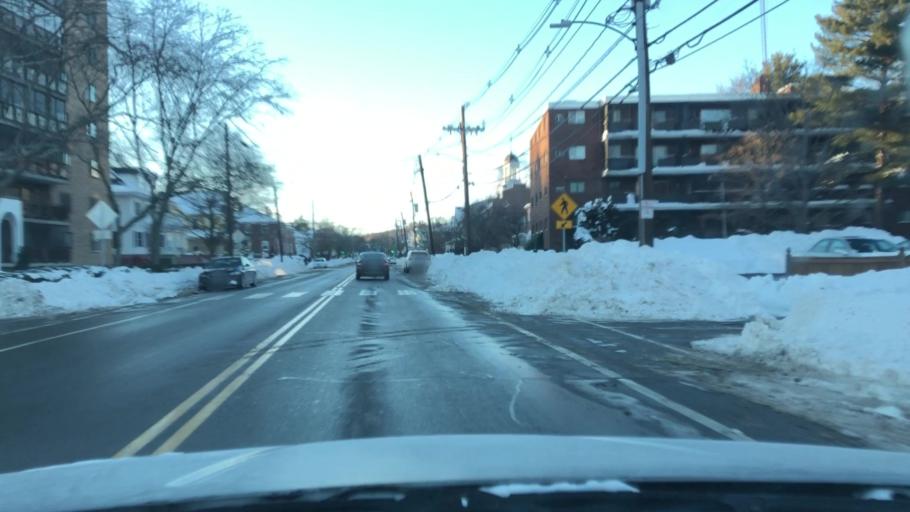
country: US
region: Massachusetts
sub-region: Middlesex County
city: Arlington
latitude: 42.4192
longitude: -71.1675
